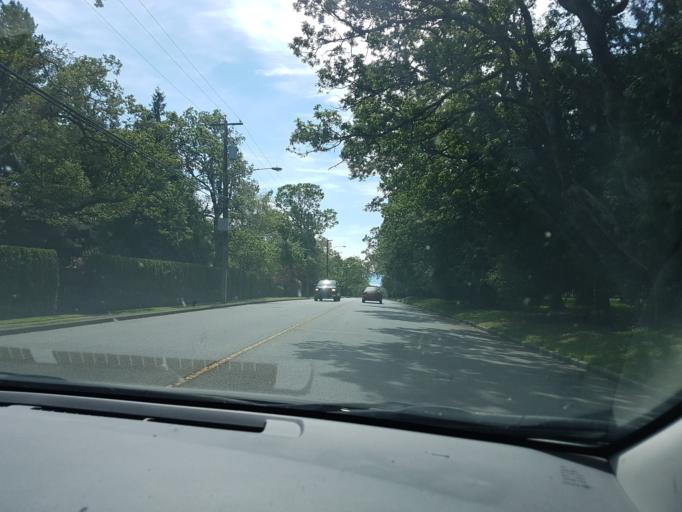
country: CA
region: British Columbia
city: Oak Bay
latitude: 48.4479
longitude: -123.3098
